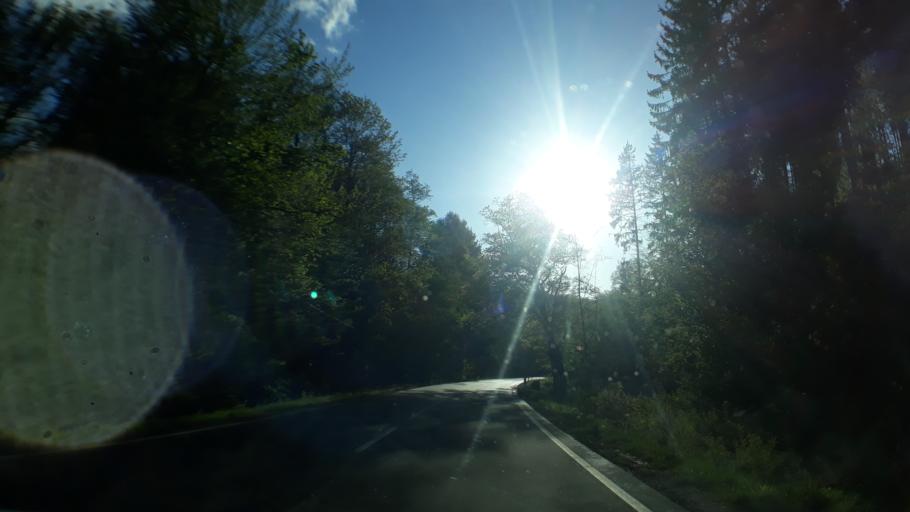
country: DE
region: North Rhine-Westphalia
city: Stolberg
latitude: 50.7097
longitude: 6.2772
